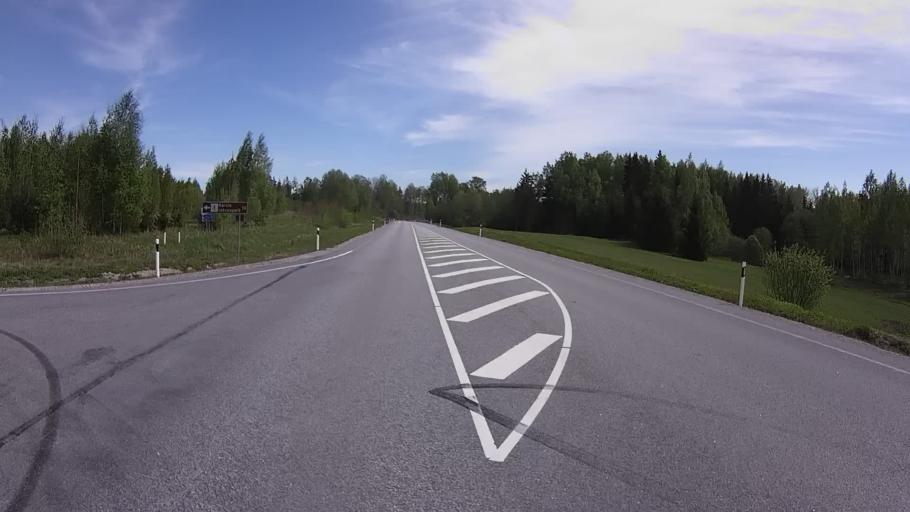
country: EE
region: Valgamaa
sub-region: Valga linn
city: Valga
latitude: 57.7519
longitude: 26.1334
